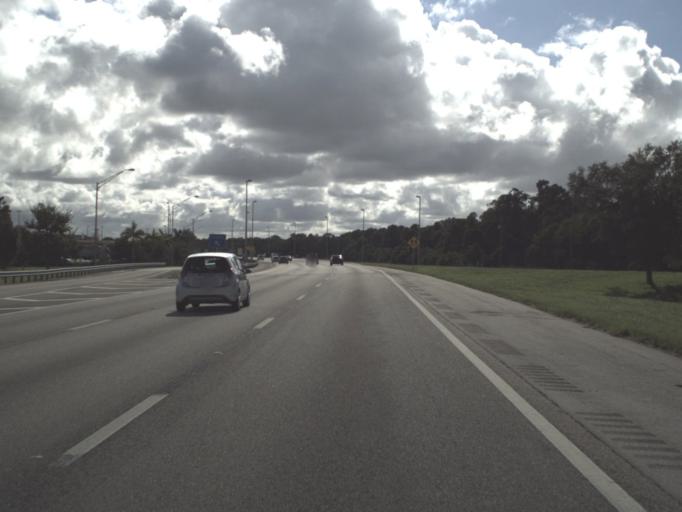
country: US
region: Florida
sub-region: Broward County
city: Coconut Creek
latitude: 26.2296
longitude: -80.1807
